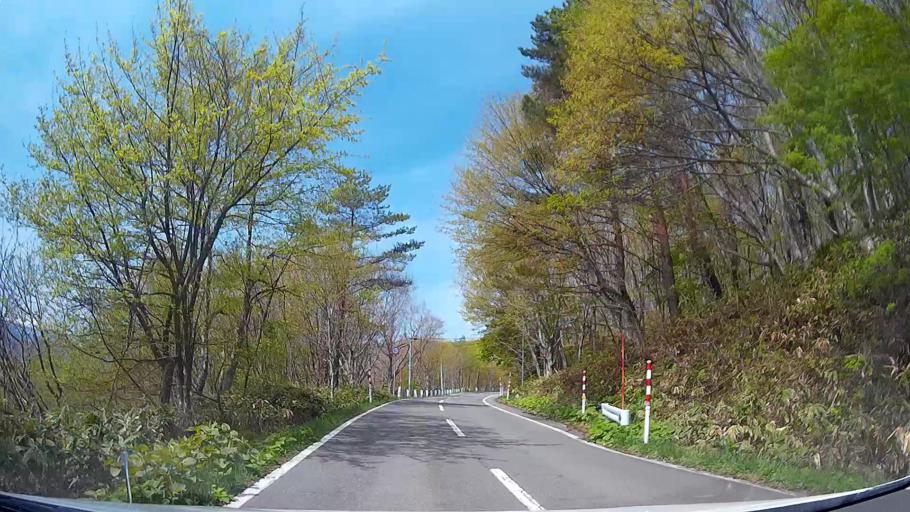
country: JP
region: Iwate
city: Shizukuishi
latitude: 39.9250
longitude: 140.9670
